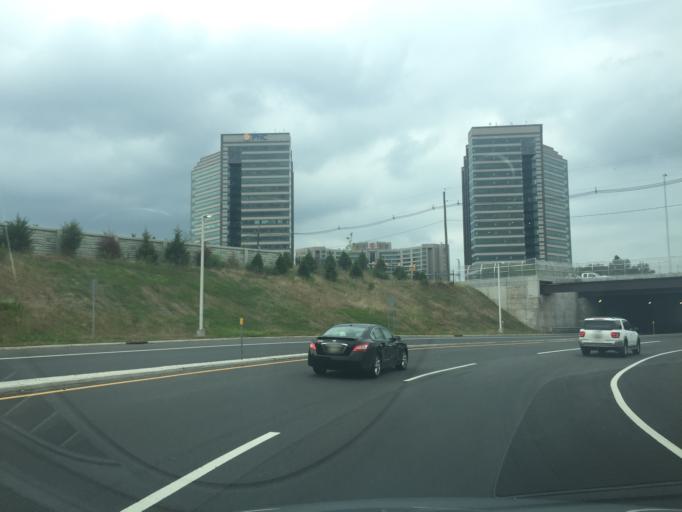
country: US
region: New Jersey
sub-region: Middlesex County
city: Highland Park
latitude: 40.4774
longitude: -74.4115
